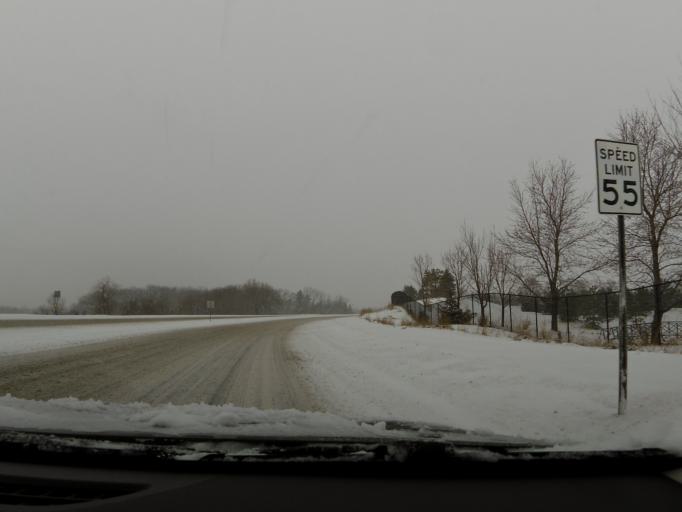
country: US
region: Minnesota
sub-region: Scott County
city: Prior Lake
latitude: 44.7248
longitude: -93.4795
